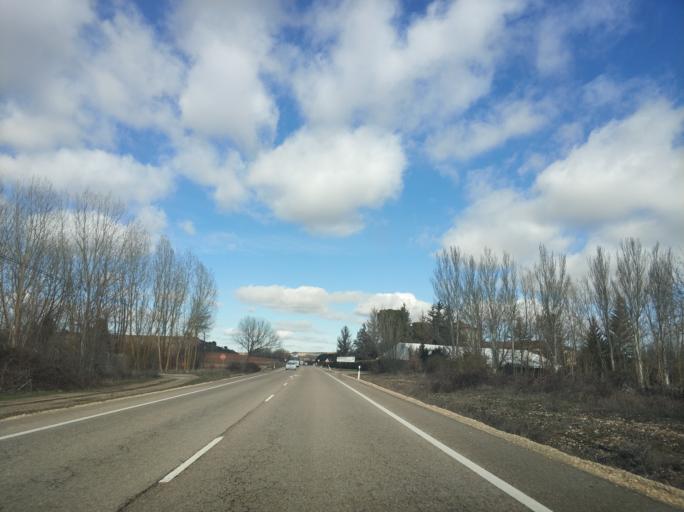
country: ES
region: Castille and Leon
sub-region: Provincia de Burgos
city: Sarracin
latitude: 42.2509
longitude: -3.6852
